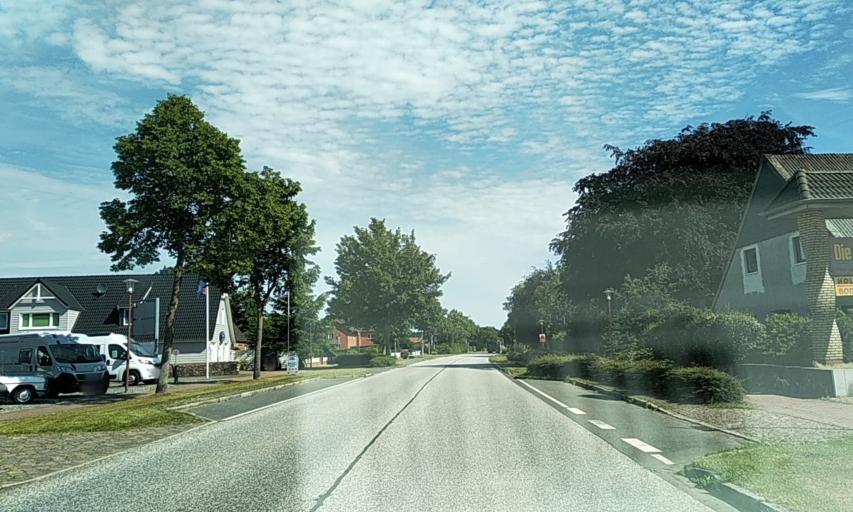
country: DE
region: Schleswig-Holstein
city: Jagel
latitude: 54.4541
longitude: 9.5370
